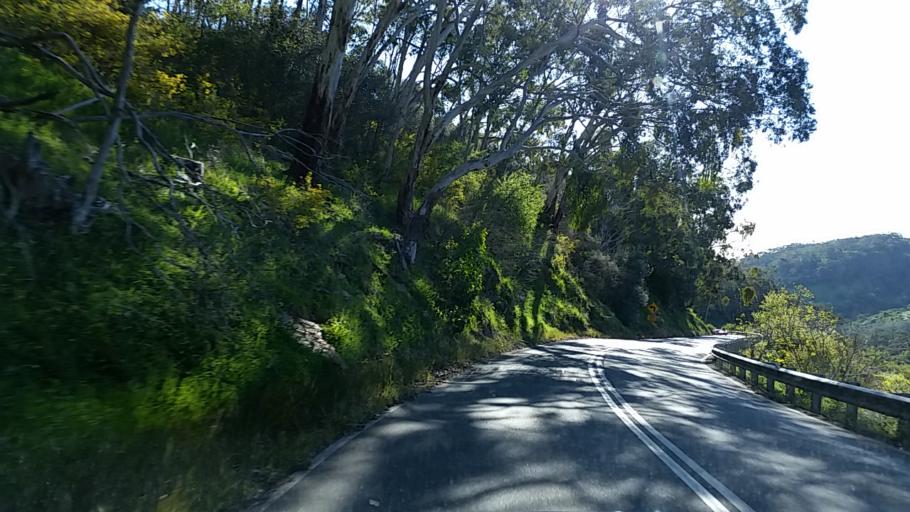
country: AU
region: South Australia
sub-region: Adelaide Hills
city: Adelaide Hills
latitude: -34.9246
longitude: 138.7216
